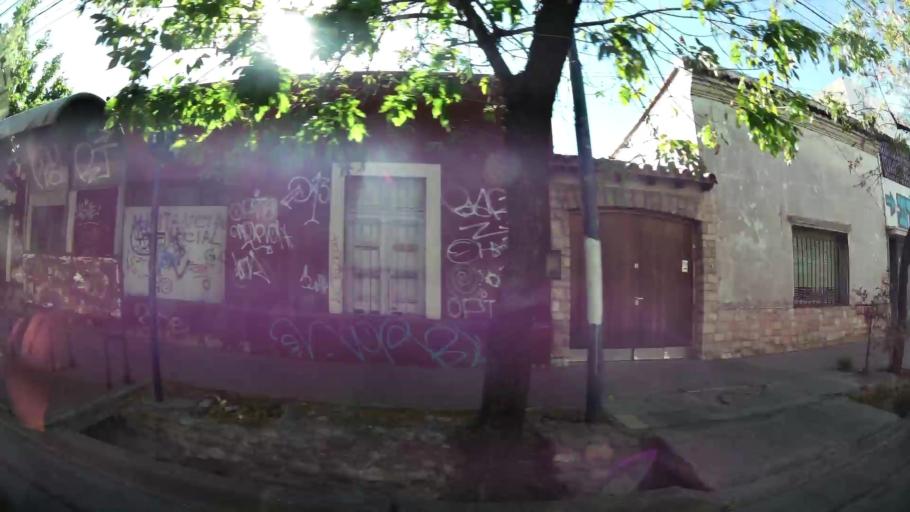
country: AR
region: Mendoza
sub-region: Departamento de Godoy Cruz
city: Godoy Cruz
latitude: -32.9133
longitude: -68.8424
